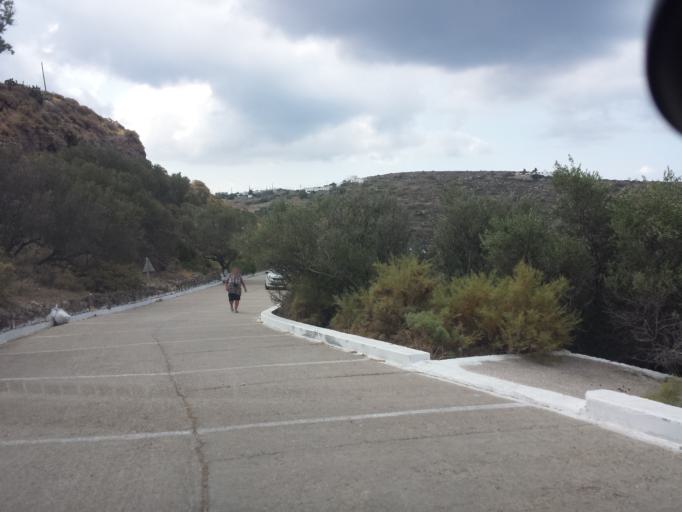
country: GR
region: South Aegean
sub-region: Nomos Kykladon
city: Milos
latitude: 36.7387
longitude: 24.4230
